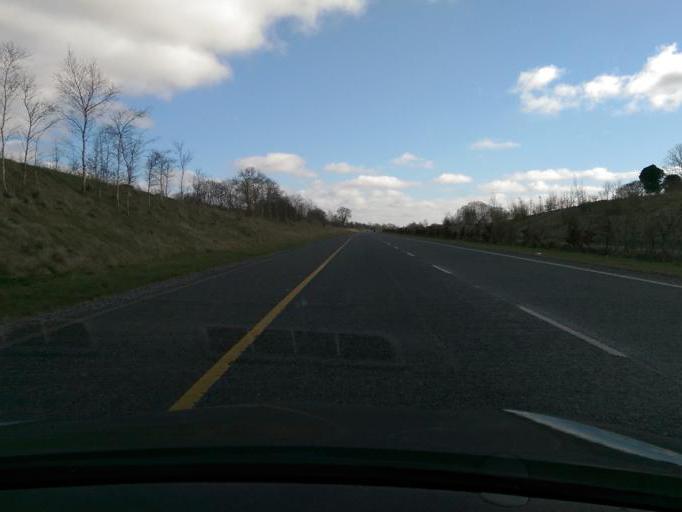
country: IE
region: Leinster
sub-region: An Mhi
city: Longwood
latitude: 53.4266
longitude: -6.9499
